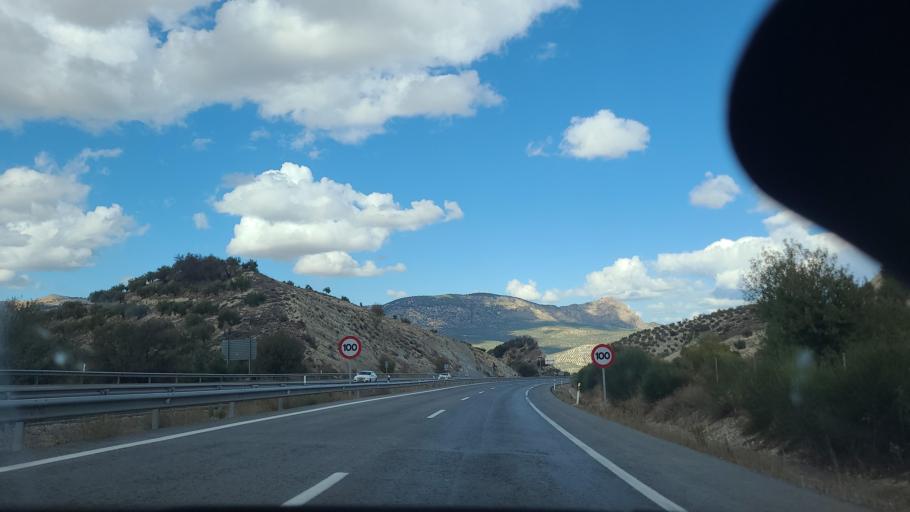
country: ES
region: Andalusia
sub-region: Provincia de Jaen
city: Campillo de Arenas
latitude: 37.5382
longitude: -3.6358
